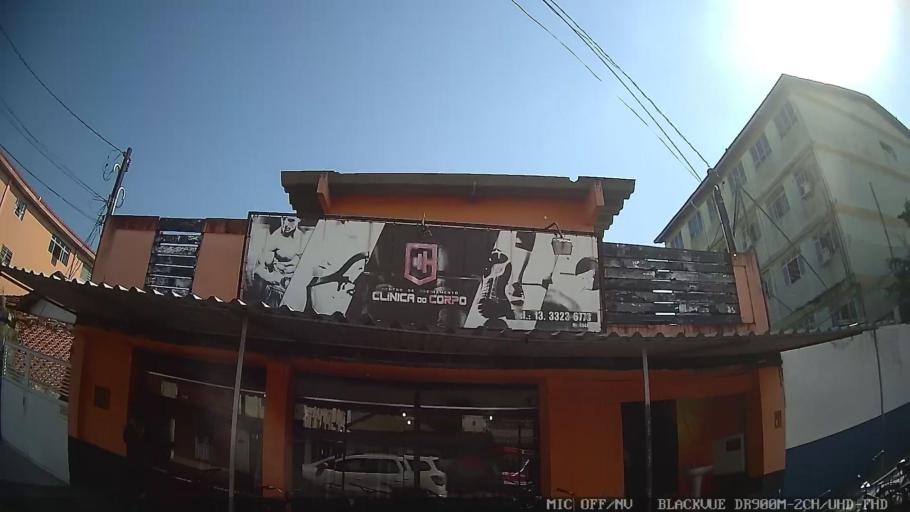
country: BR
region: Sao Paulo
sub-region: Santos
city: Santos
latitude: -23.9409
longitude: -46.3026
